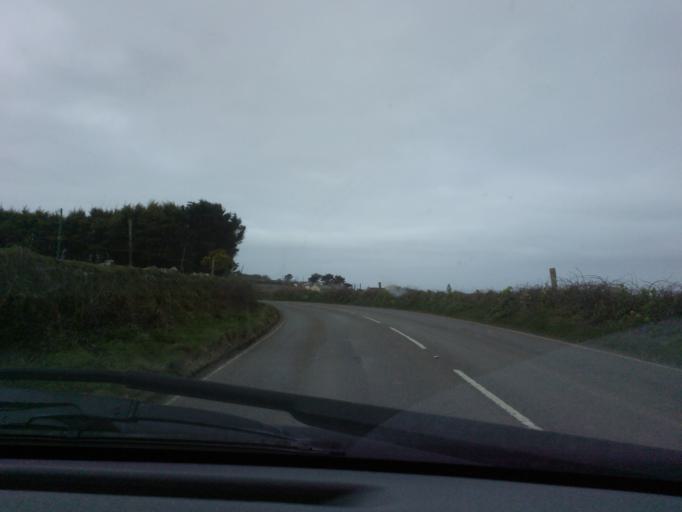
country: GB
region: England
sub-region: Cornwall
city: Saint Just
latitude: 50.1210
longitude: -5.6722
